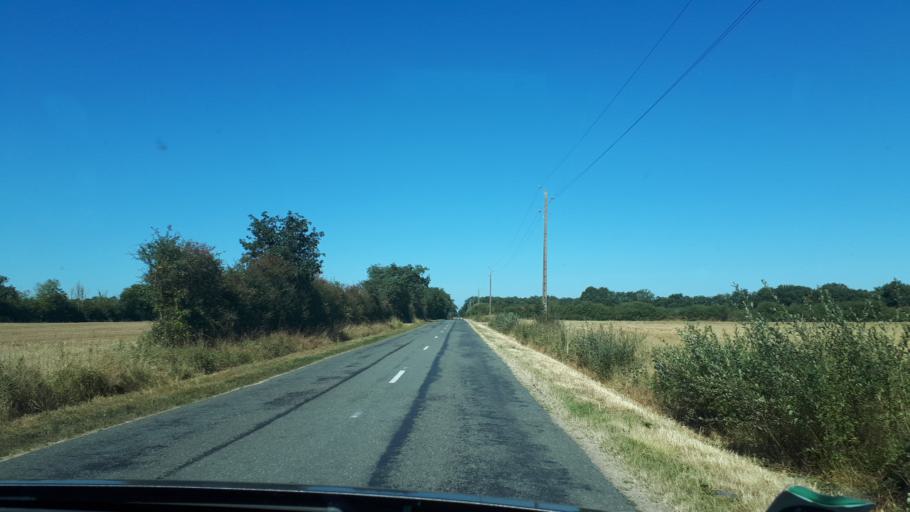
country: FR
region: Centre
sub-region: Departement du Loiret
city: Coullons
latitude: 47.6290
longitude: 2.4765
